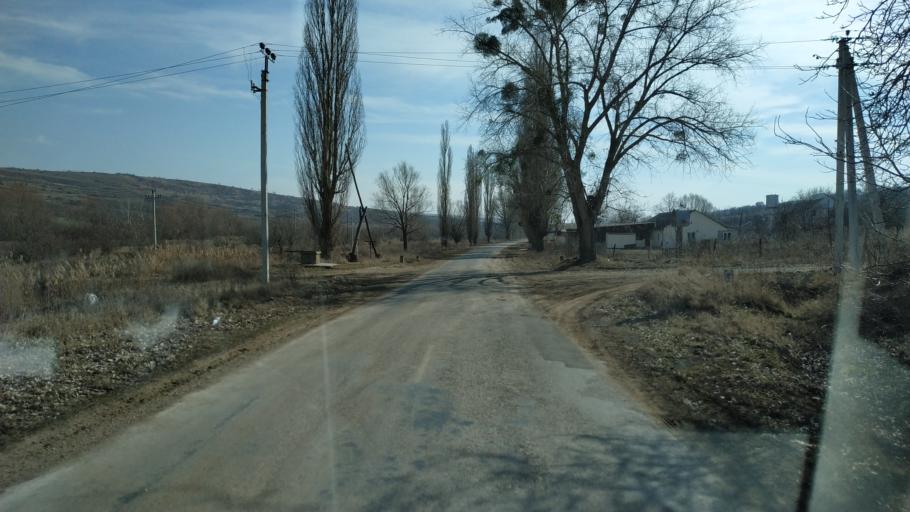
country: MD
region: Nisporeni
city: Nisporeni
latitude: 47.1619
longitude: 28.1030
